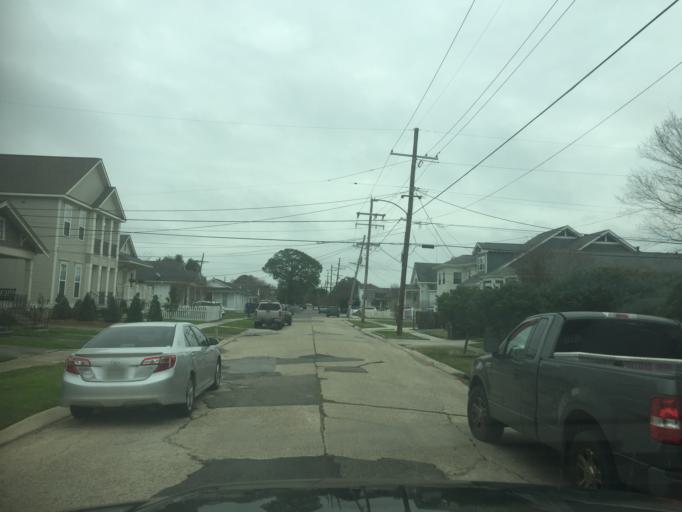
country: US
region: Louisiana
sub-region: Jefferson Parish
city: Metairie
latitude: 30.0027
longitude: -90.1068
